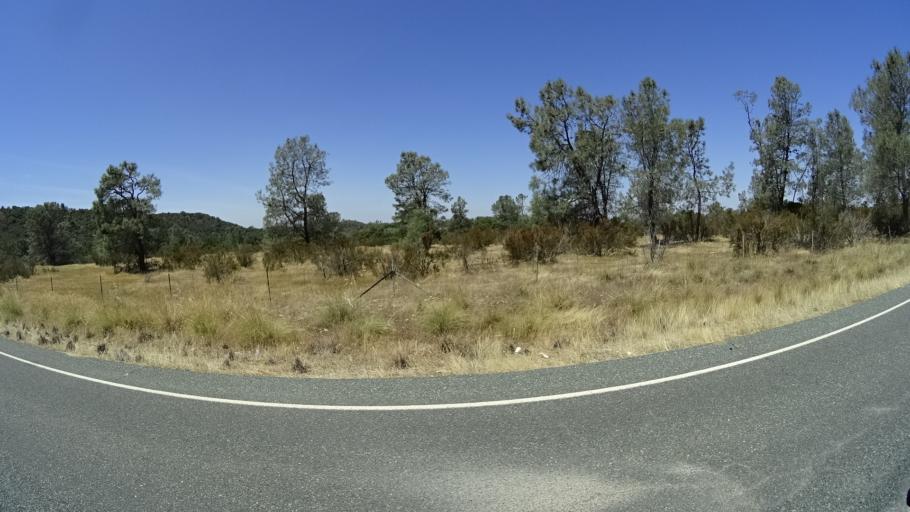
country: US
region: California
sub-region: Calaveras County
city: Valley Springs
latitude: 38.1980
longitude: -120.9057
